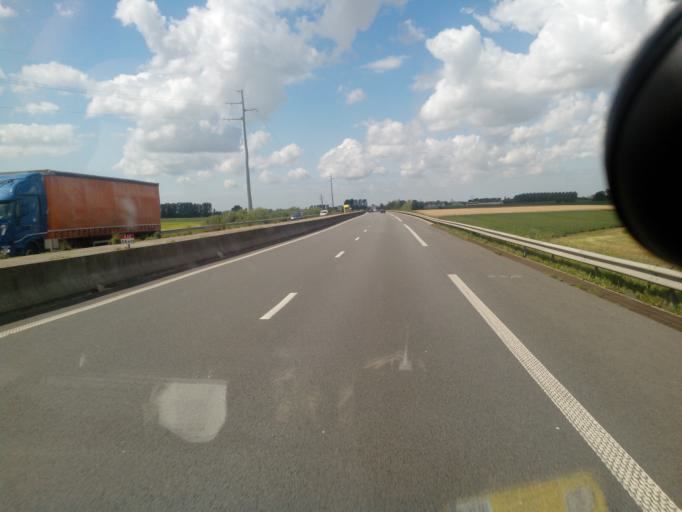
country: FR
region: Nord-Pas-de-Calais
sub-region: Departement du Nord
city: Herzeele
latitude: 50.8929
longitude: 2.5077
